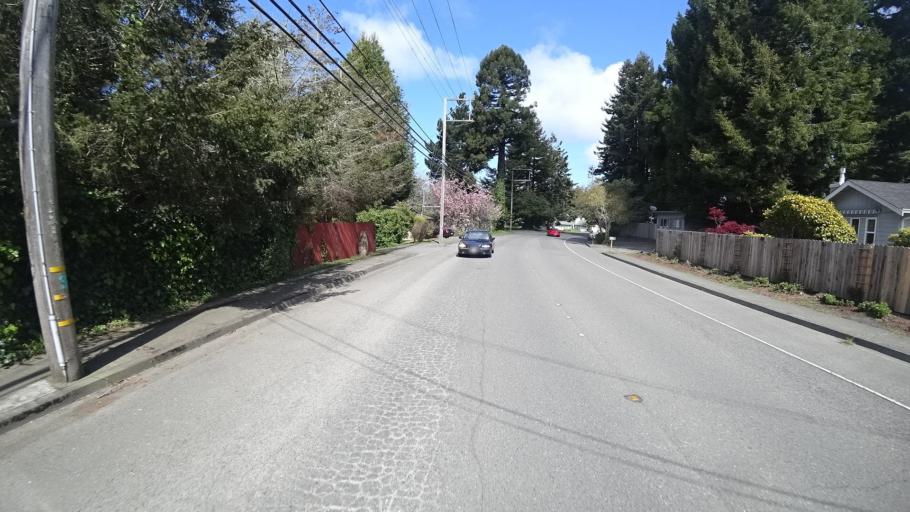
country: US
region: California
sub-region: Humboldt County
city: Cutten
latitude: 40.7592
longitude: -124.1537
